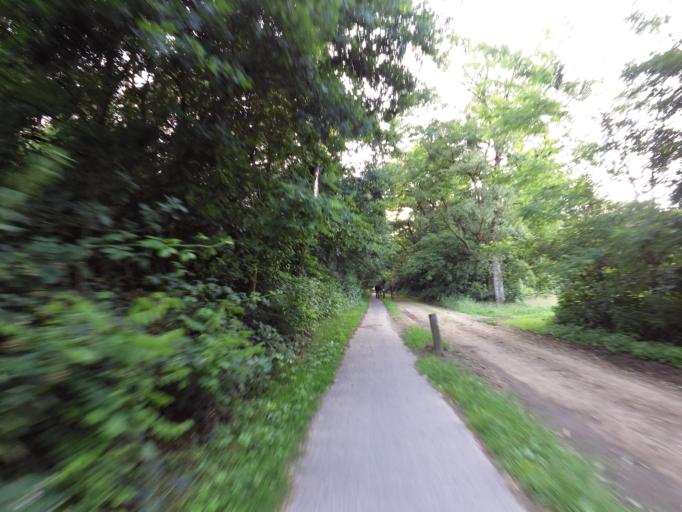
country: NL
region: Gelderland
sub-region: Gemeente Doesburg
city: Doesburg
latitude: 52.0014
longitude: 6.2143
